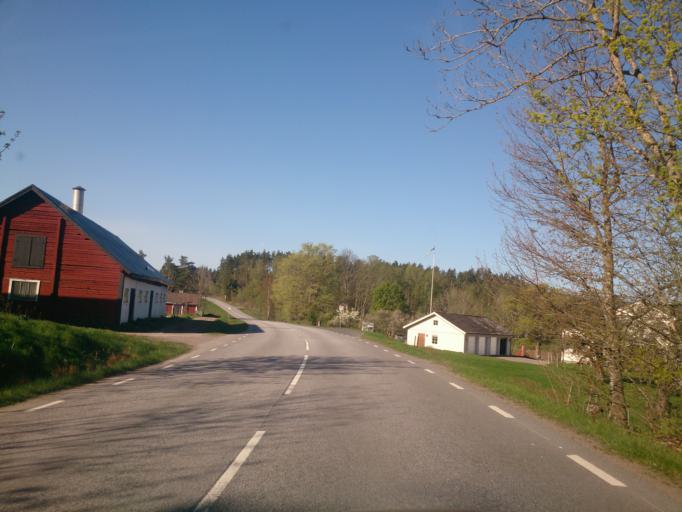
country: SE
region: OEstergoetland
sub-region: Linkopings Kommun
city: Berg
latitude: 58.5280
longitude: 15.5560
